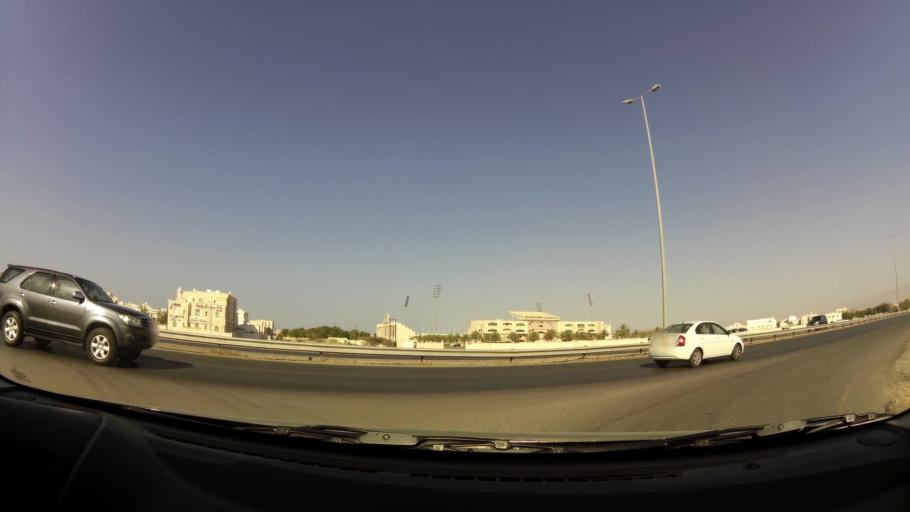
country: OM
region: Muhafazat Masqat
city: As Sib al Jadidah
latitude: 23.6193
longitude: 58.2131
